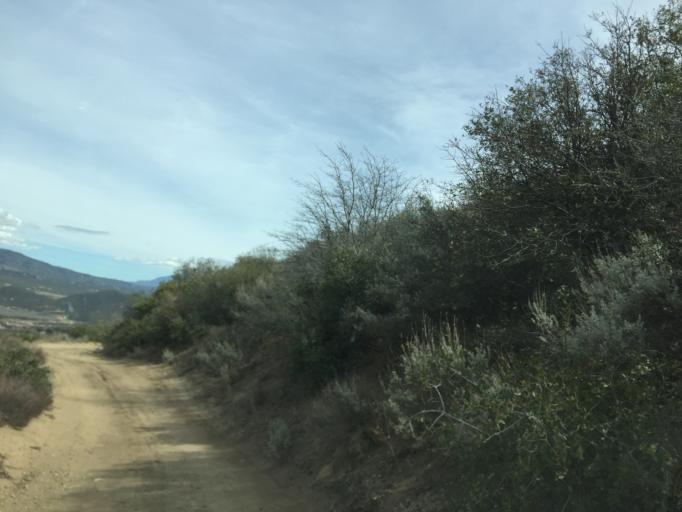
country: US
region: California
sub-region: Riverside County
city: Anza
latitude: 33.5960
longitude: -116.7798
